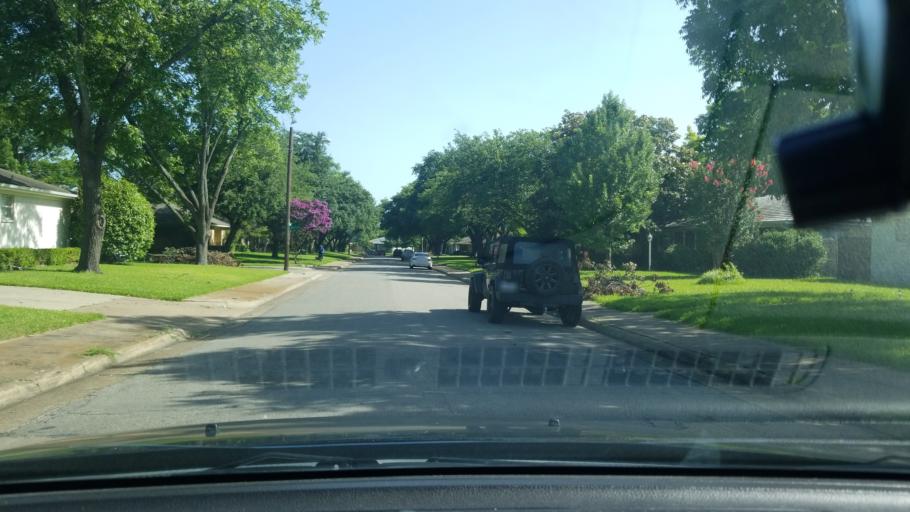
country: US
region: Texas
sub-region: Dallas County
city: Mesquite
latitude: 32.8072
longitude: -96.6742
